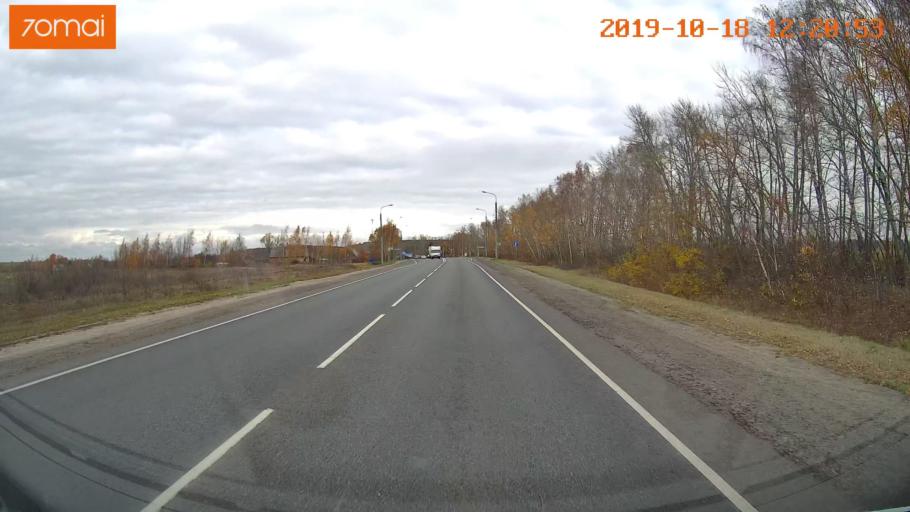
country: RU
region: Rjazan
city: Bagramovo
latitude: 54.5044
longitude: 39.4855
